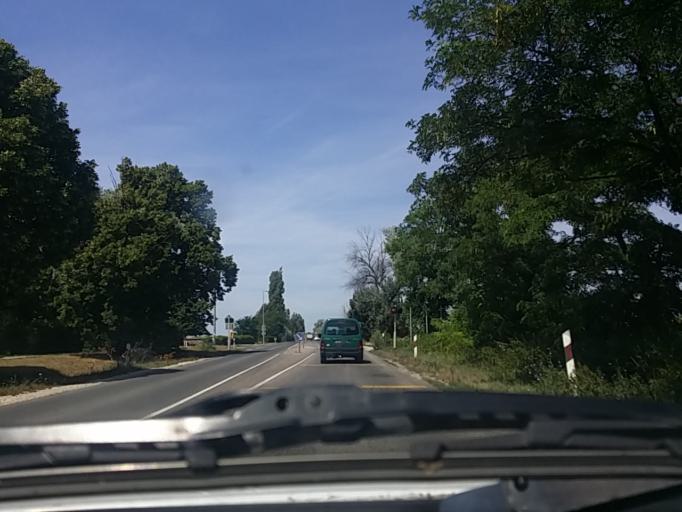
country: HU
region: Pest
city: Solymar
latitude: 47.6010
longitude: 18.9587
